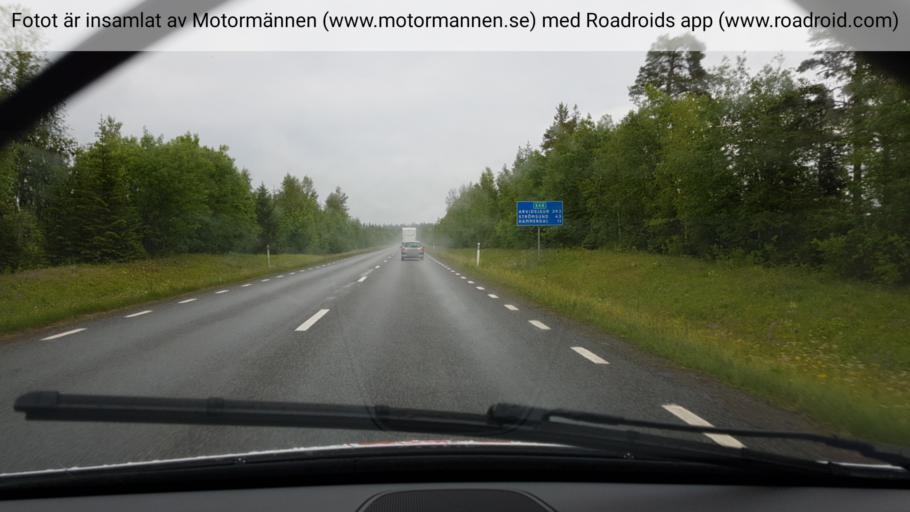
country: SE
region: Jaemtland
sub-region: Stroemsunds Kommun
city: Stroemsund
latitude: 63.5086
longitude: 15.2824
